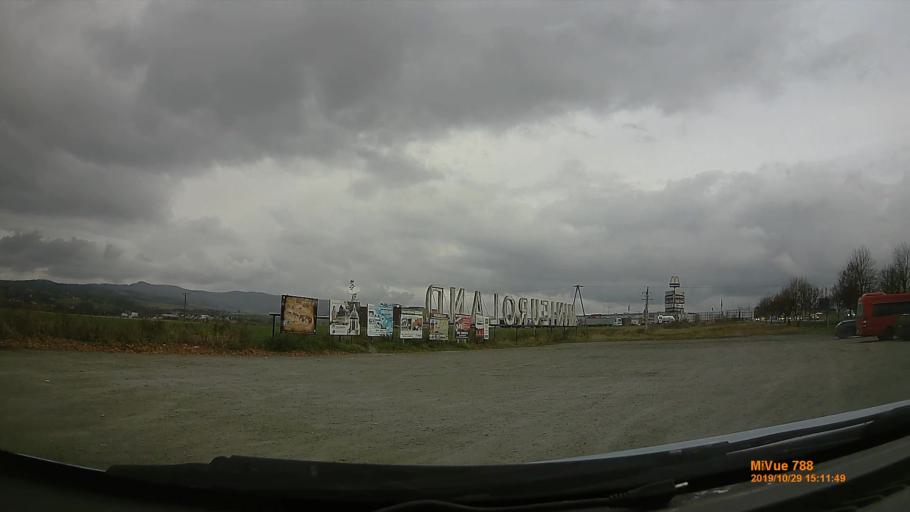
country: PL
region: Lower Silesian Voivodeship
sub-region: Powiat klodzki
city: Klodzko
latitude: 50.4550
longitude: 16.6327
